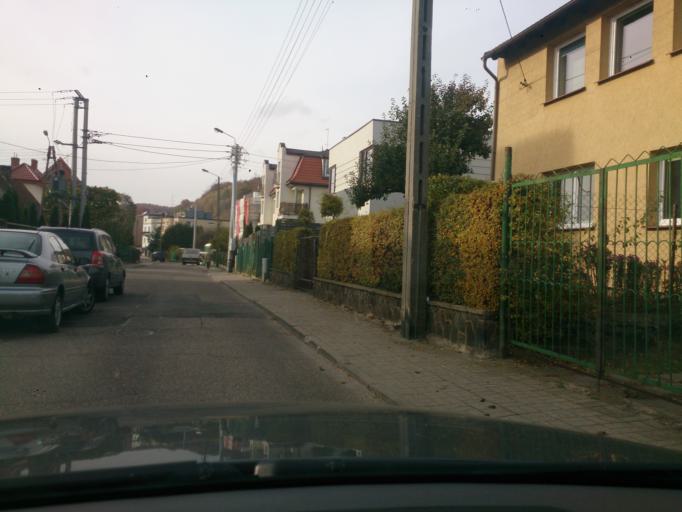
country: PL
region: Pomeranian Voivodeship
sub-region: Gdynia
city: Gdynia
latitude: 54.4865
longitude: 18.5229
